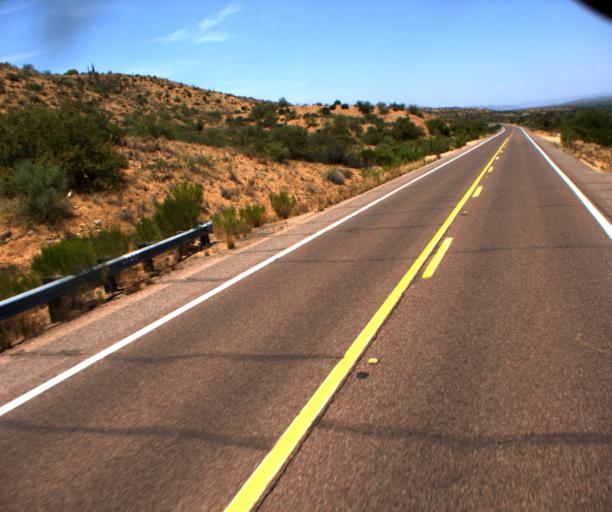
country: US
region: Arizona
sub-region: Gila County
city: Tonto Basin
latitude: 33.7694
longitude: -111.2594
